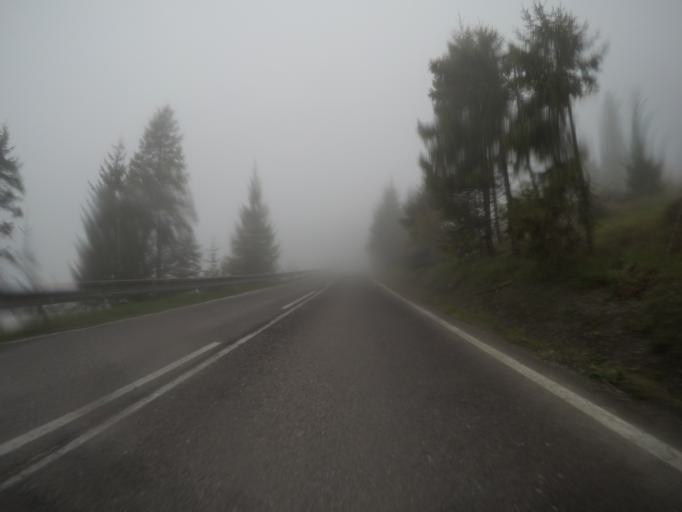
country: SK
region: Presovsky
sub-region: Okres Poprad
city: Strba
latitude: 49.1066
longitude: 20.0656
